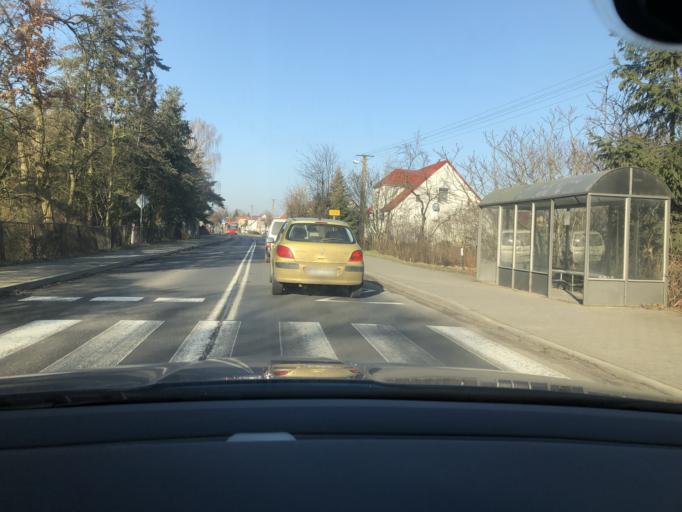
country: PL
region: Greater Poland Voivodeship
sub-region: Powiat szamotulski
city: Duszniki
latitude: 52.4418
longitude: 16.4098
